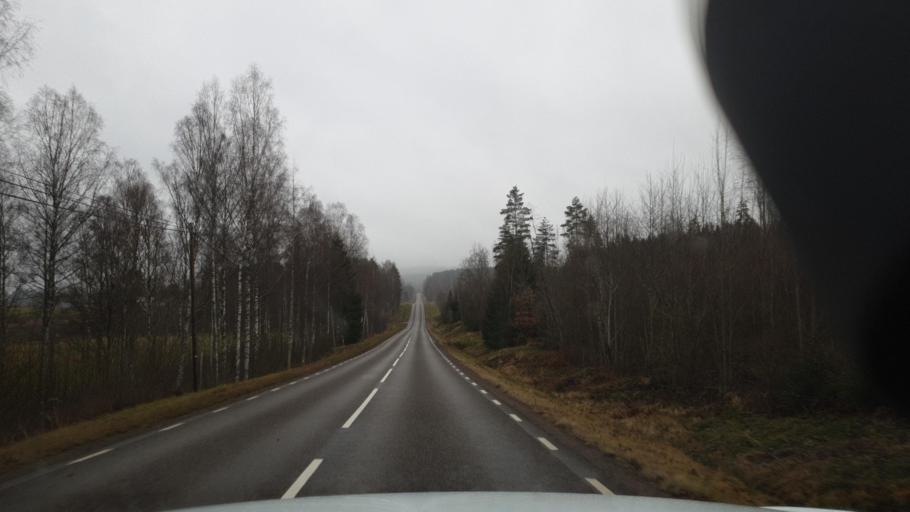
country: SE
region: Vaermland
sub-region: Eda Kommun
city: Amotfors
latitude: 59.7501
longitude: 12.3693
